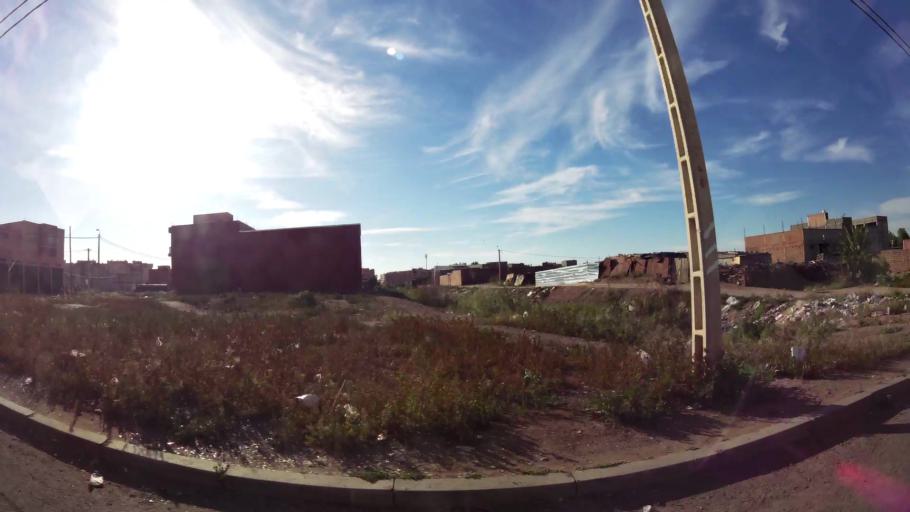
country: MA
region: Marrakech-Tensift-Al Haouz
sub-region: Marrakech
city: Marrakesh
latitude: 31.6837
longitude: -8.0589
